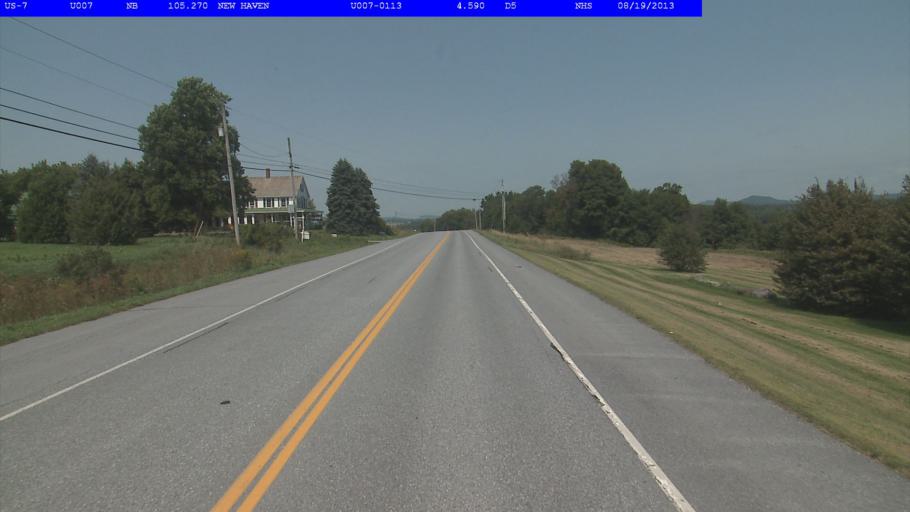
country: US
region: Vermont
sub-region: Addison County
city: Middlebury (village)
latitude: 44.1114
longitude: -73.1750
